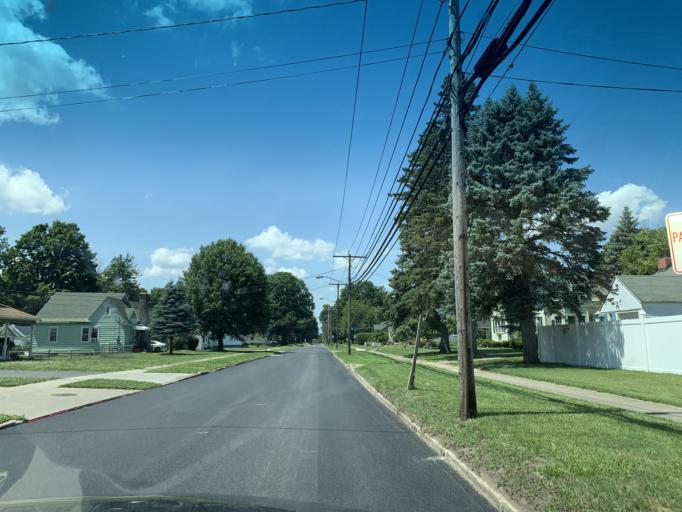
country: US
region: New York
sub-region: Oneida County
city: Utica
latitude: 43.1195
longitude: -75.2188
